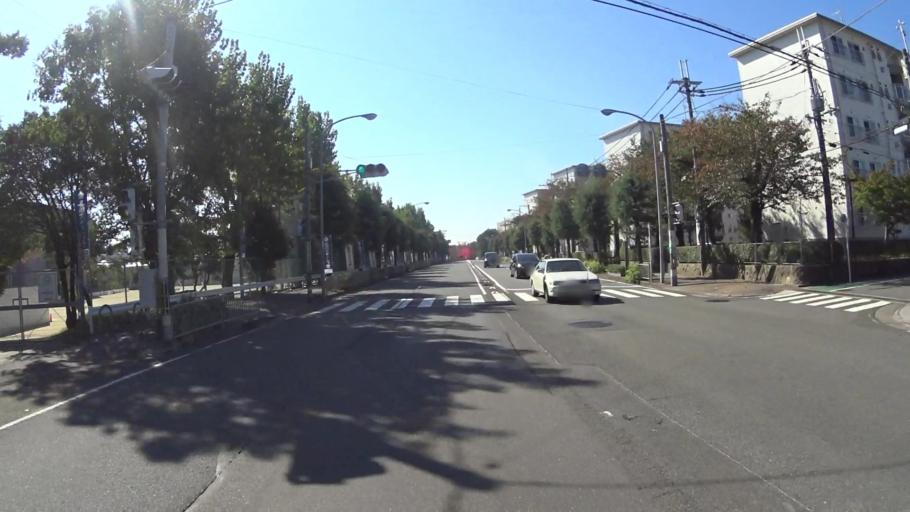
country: JP
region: Kyoto
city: Muko
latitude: 34.9298
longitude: 135.6895
